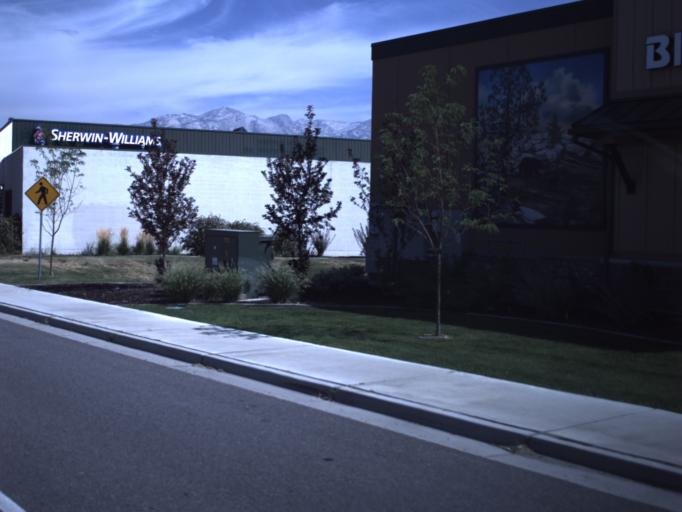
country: US
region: Utah
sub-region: Utah County
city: American Fork
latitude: 40.3803
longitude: -111.8135
